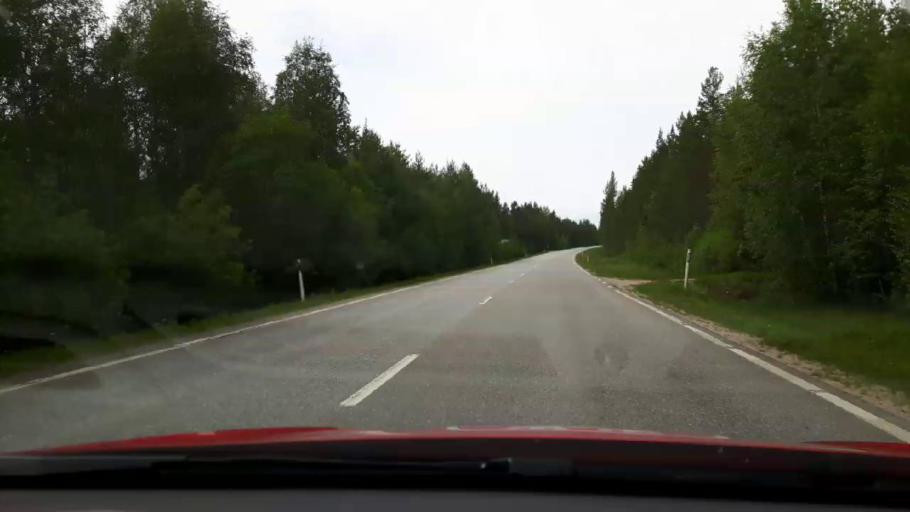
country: SE
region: Jaemtland
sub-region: Harjedalens Kommun
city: Sveg
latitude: 62.0469
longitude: 14.3337
